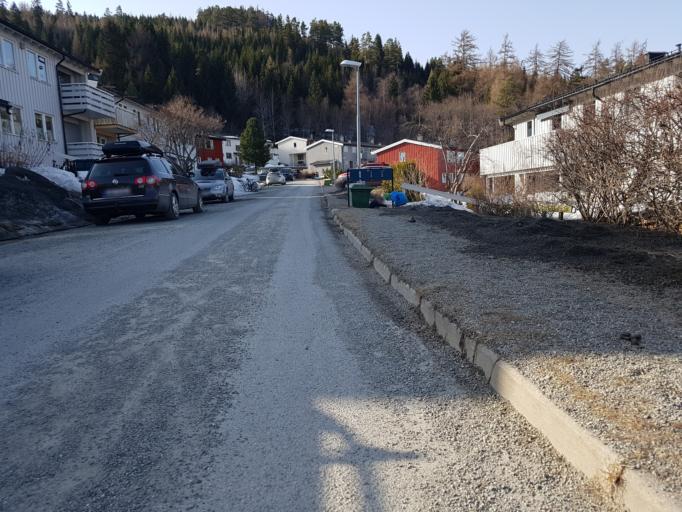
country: NO
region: Sor-Trondelag
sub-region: Trondheim
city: Trondheim
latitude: 63.4293
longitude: 10.3465
